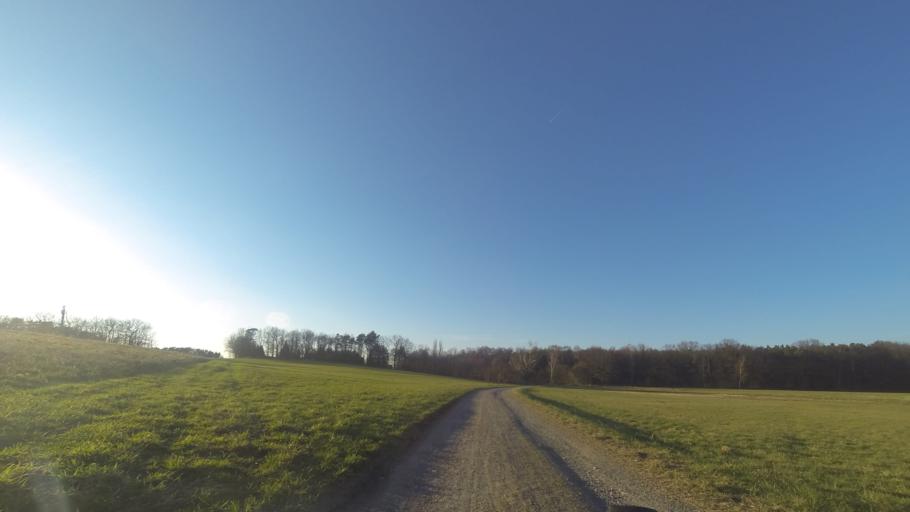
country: DE
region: Saxony
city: Albertstadt
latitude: 51.1354
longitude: 13.7592
